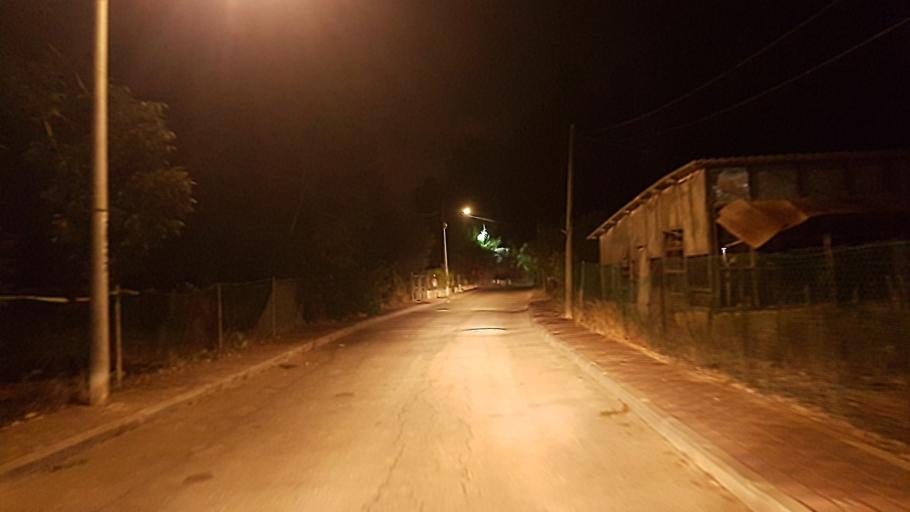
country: IL
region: Central District
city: Hod HaSharon
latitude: 32.1481
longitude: 34.9000
